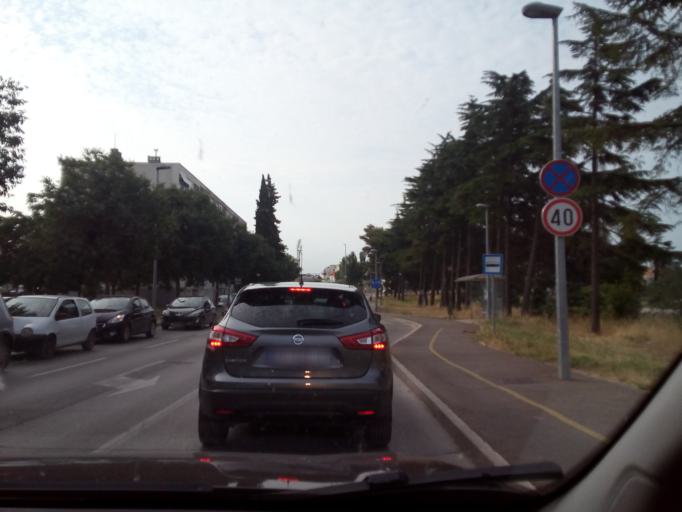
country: HR
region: Zadarska
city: Zadar
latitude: 44.1170
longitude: 15.2429
